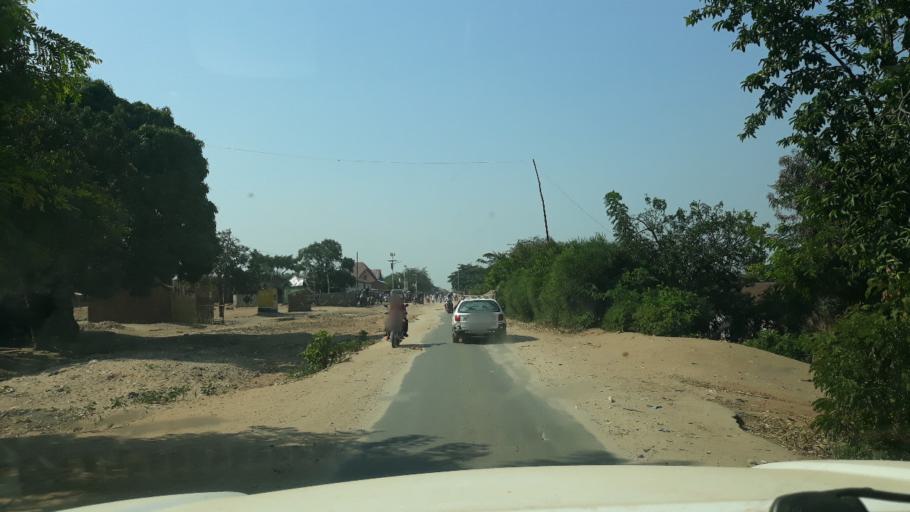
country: CD
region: South Kivu
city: Uvira
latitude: -3.2384
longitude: 29.1624
